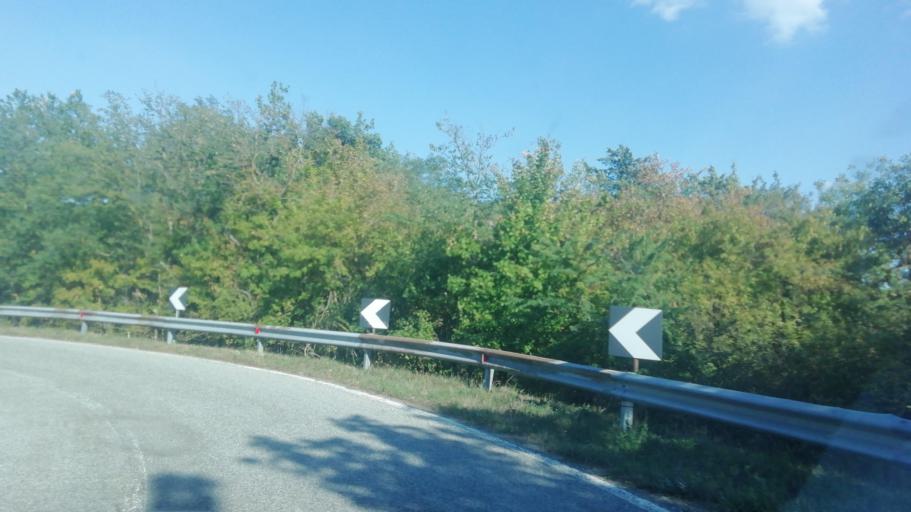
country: IT
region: The Marches
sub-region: Provincia di Pesaro e Urbino
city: Cagli
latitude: 43.5381
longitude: 12.6974
